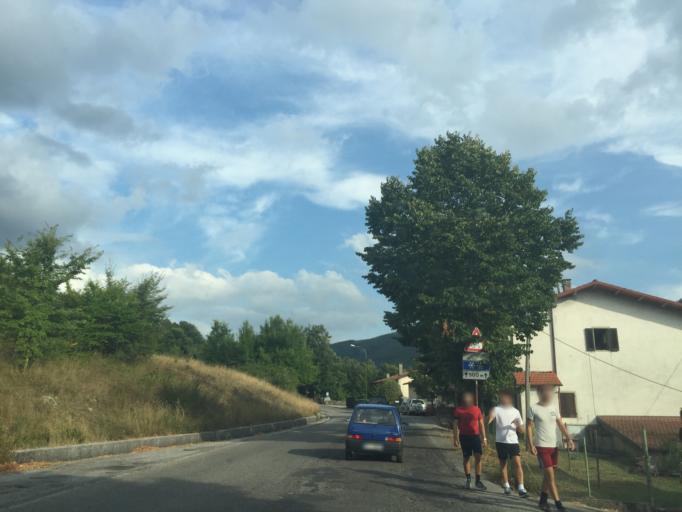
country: IT
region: Tuscany
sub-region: Provincia di Pistoia
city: San Marcello Pistoiese
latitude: 44.0530
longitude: 10.8022
